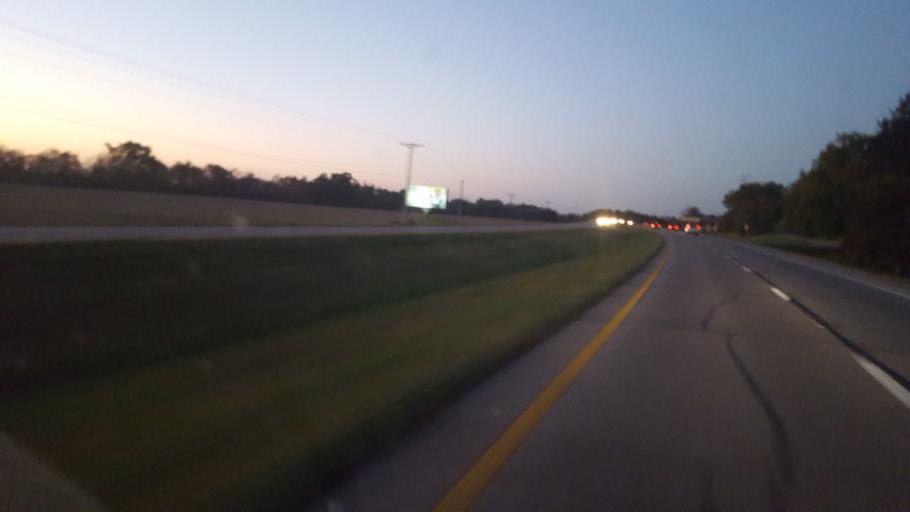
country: US
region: Ohio
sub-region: Ross County
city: Kingston
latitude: 39.5029
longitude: -82.9737
